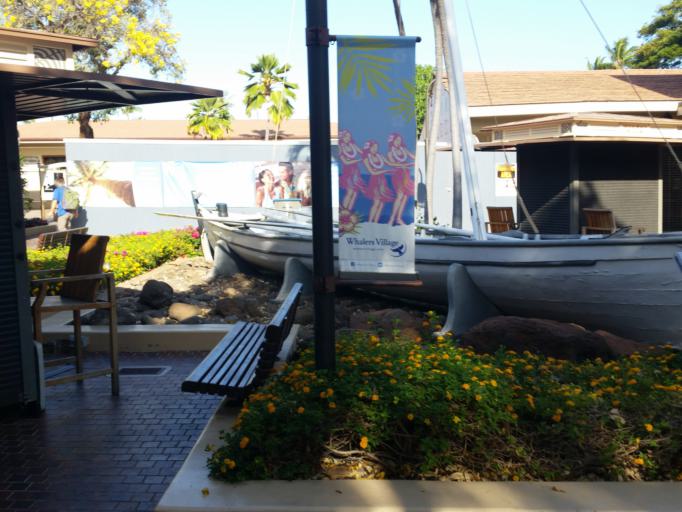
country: US
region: Hawaii
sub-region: Maui County
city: Ka'anapali
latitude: 20.9216
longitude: -156.6945
